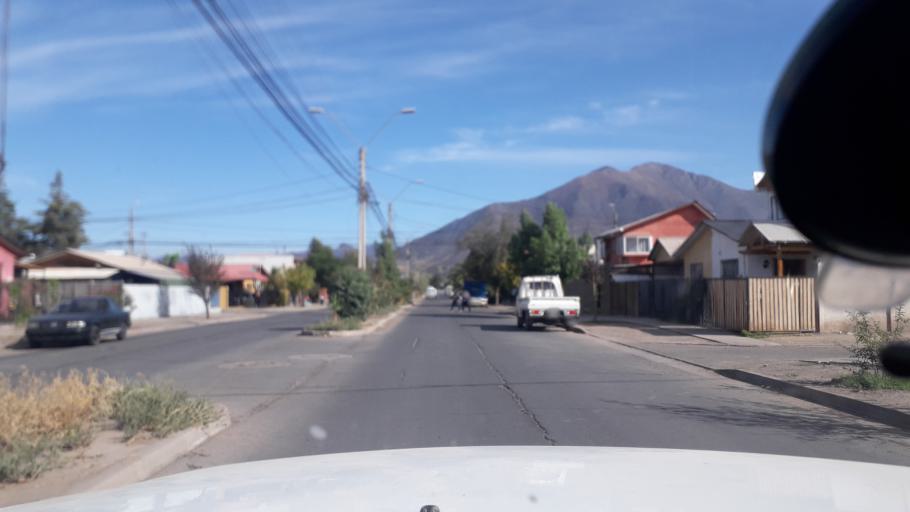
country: CL
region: Valparaiso
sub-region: Provincia de San Felipe
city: San Felipe
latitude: -32.7552
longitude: -70.7125
